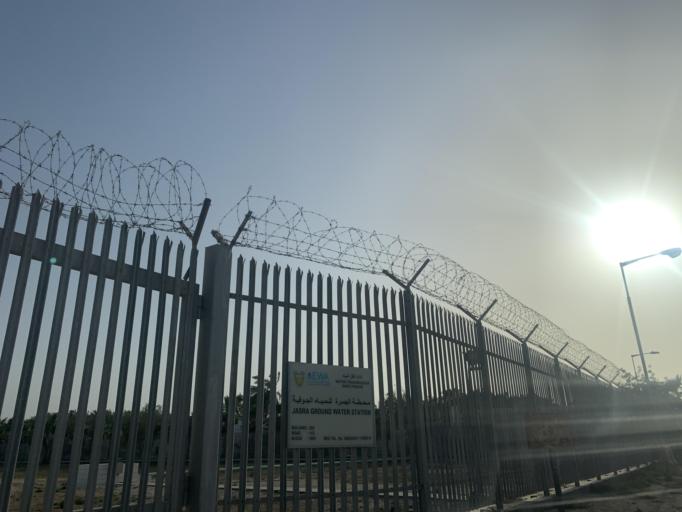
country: BH
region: Central Governorate
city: Madinat Hamad
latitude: 26.1760
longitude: 50.4525
